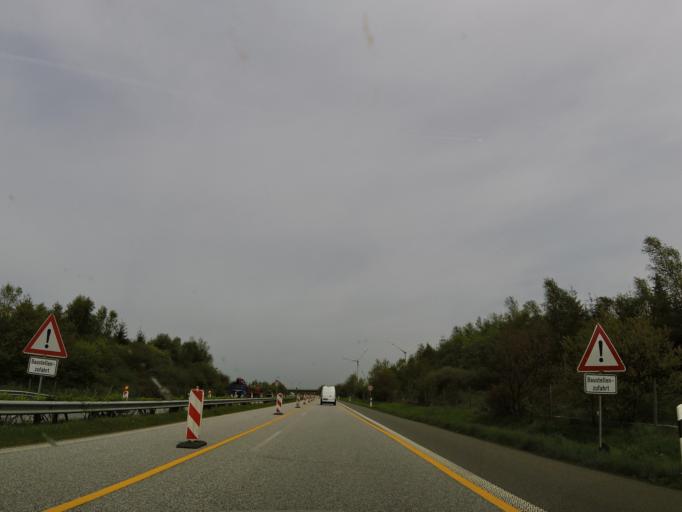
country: DE
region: Schleswig-Holstein
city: Tensbuttel-Rost
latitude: 54.0949
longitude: 9.2662
